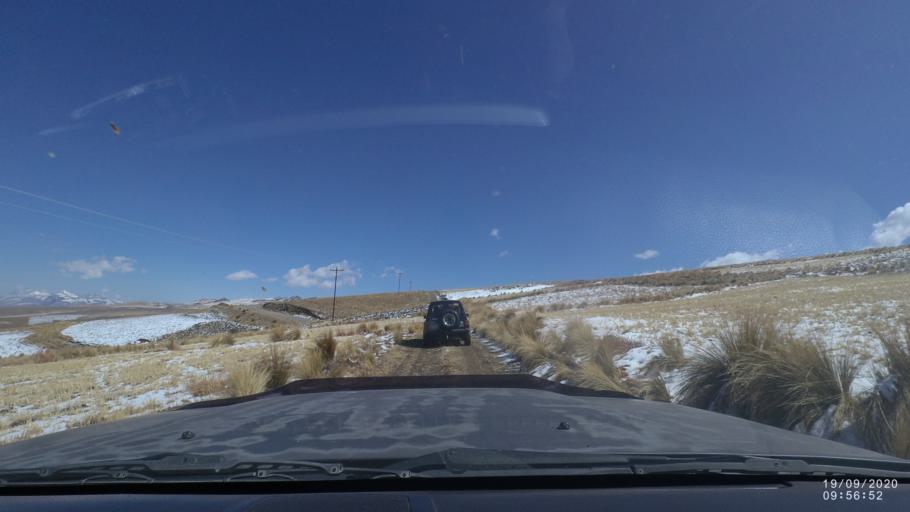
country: BO
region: Cochabamba
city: Cochabamba
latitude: -17.3122
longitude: -66.0832
